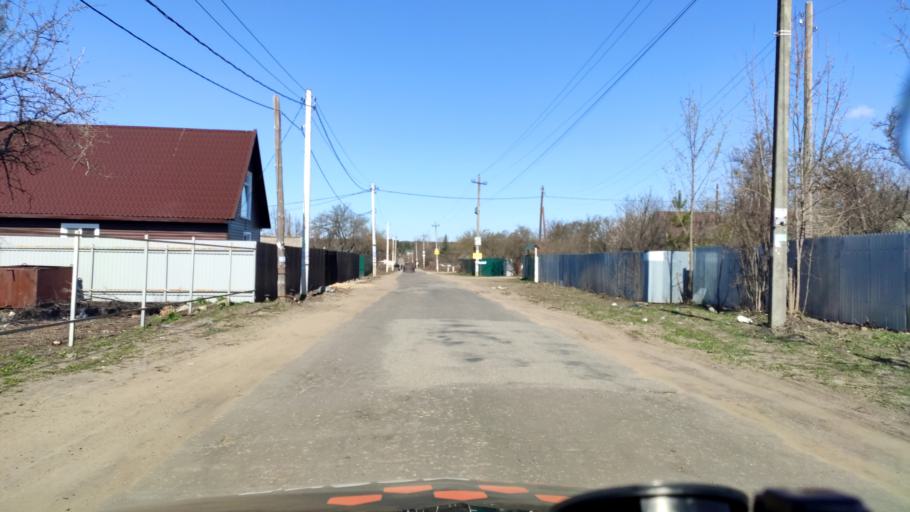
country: RU
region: Voronezj
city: Shilovo
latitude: 51.5999
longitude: 39.1442
